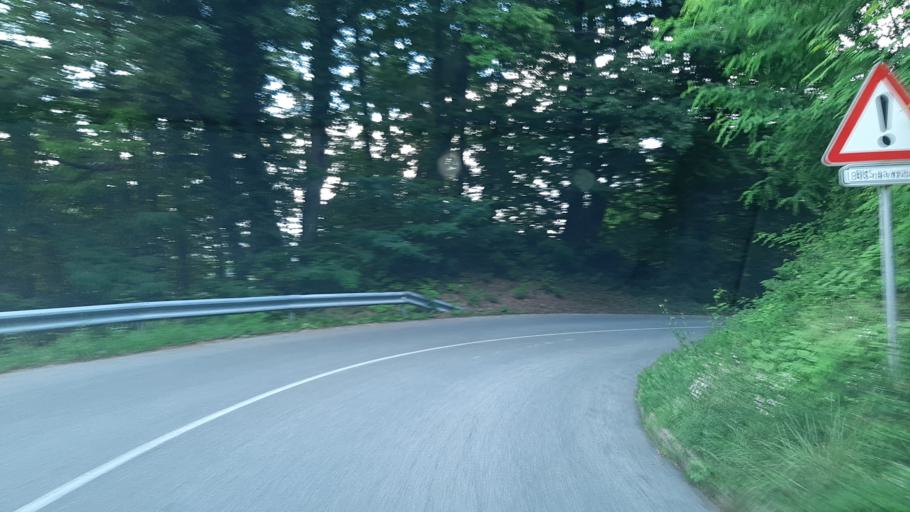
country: SI
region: Dobje
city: Dobje pri Planini
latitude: 46.1442
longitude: 15.4488
